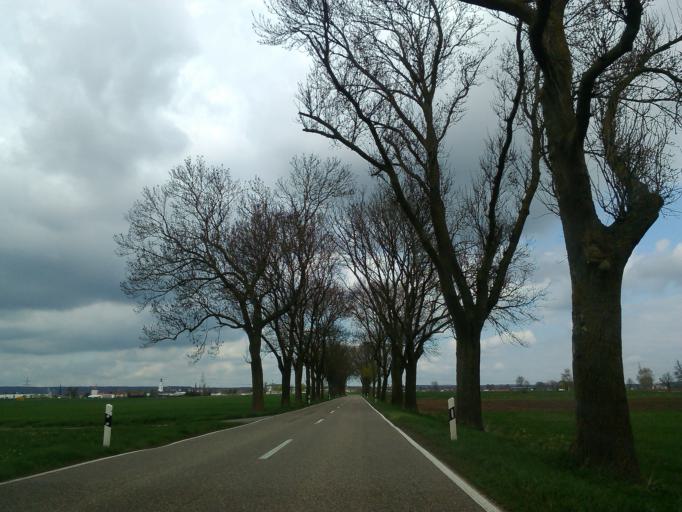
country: DE
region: Baden-Wuerttemberg
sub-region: Tuebingen Region
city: Langenau
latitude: 48.4851
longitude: 10.1407
